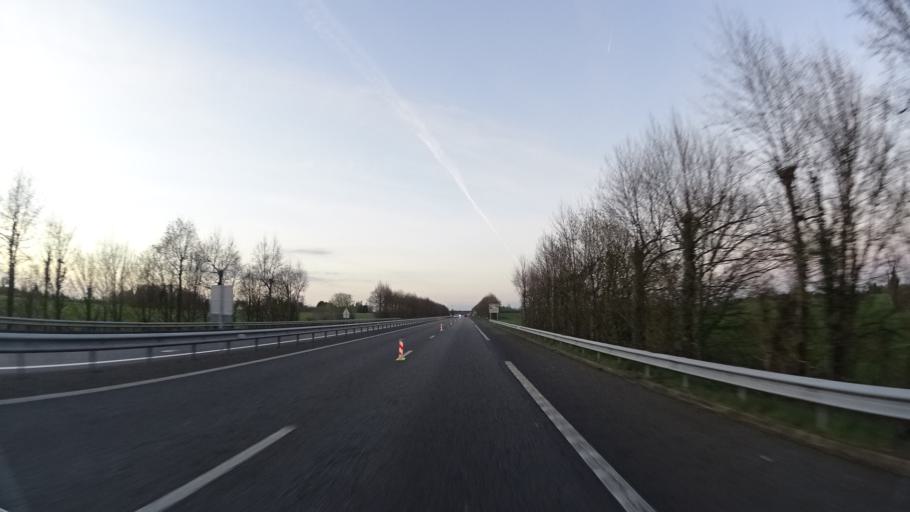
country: FR
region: Brittany
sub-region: Departement d'Ille-et-Vilaine
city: Plelan-le-Grand
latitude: 47.9827
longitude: -2.0976
